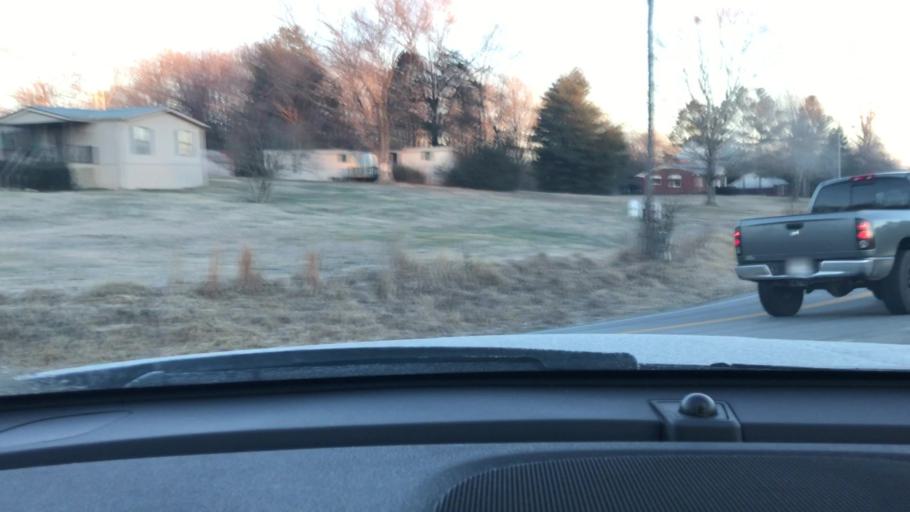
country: US
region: Tennessee
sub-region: Dickson County
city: Charlotte
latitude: 36.2115
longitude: -87.2611
